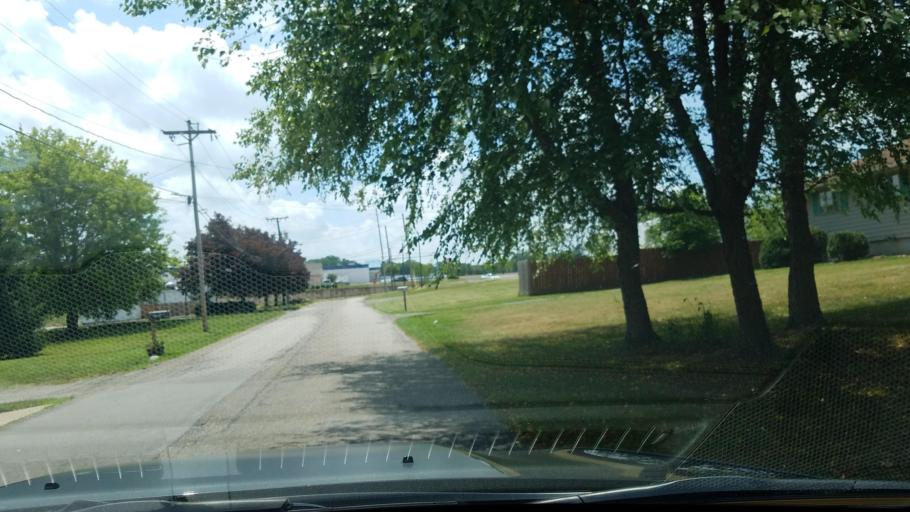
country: US
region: Ohio
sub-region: Trumbull County
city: Bolindale
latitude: 41.2203
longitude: -80.7775
